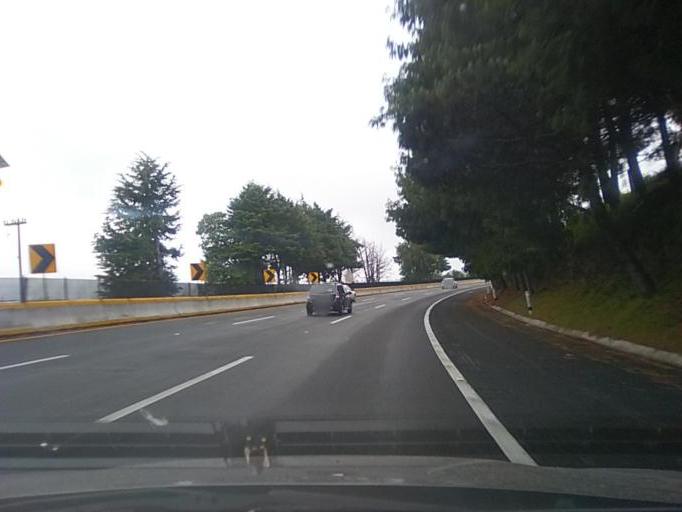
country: MX
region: Mexico City
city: Xochimilco
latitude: 19.1709
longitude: -99.1498
